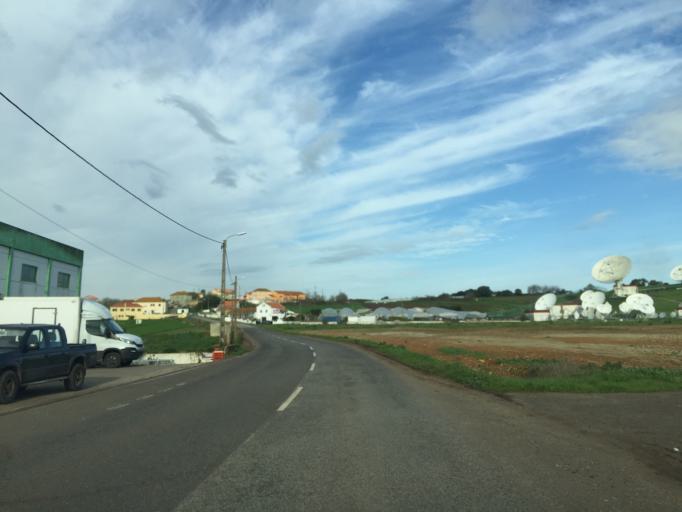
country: PT
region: Lisbon
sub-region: Sintra
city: Almargem
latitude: 38.8655
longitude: -9.2825
